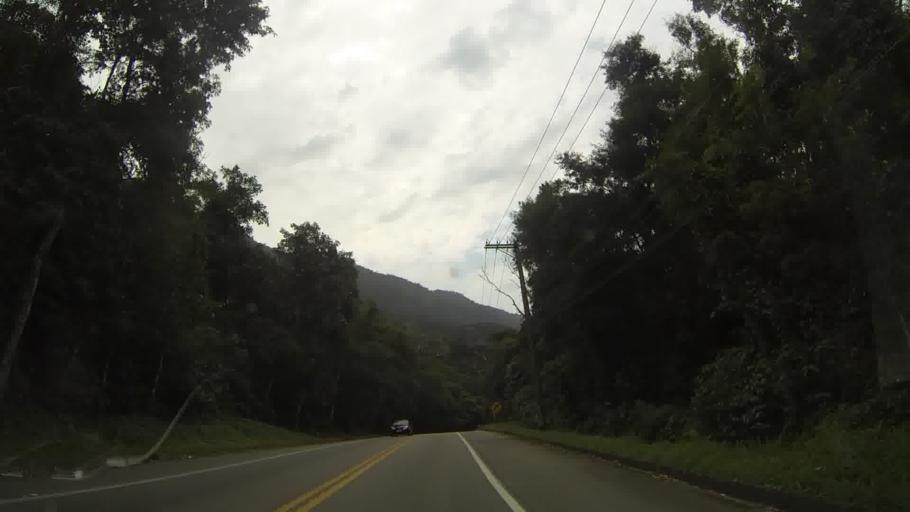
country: BR
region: Sao Paulo
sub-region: Sao Sebastiao
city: Sao Sebastiao
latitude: -23.8204
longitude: -45.4768
